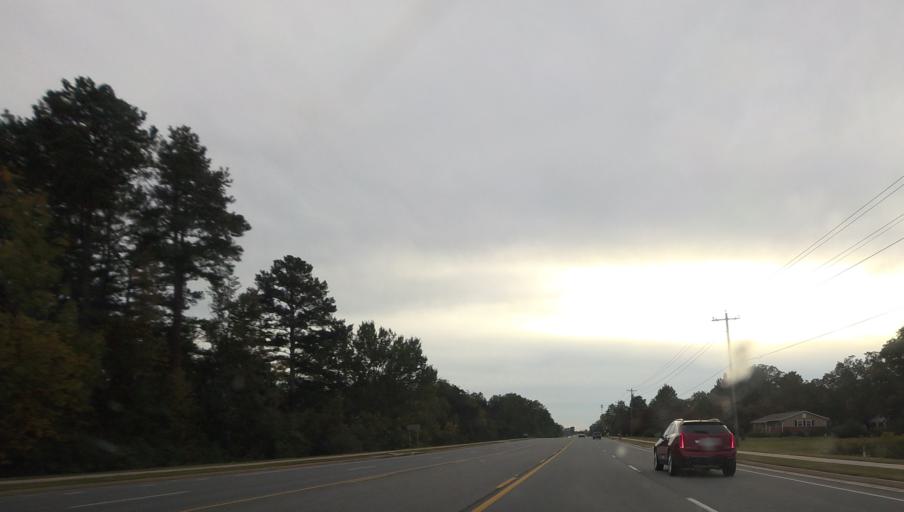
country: US
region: Georgia
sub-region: Houston County
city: Perry
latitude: 32.4831
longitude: -83.6939
